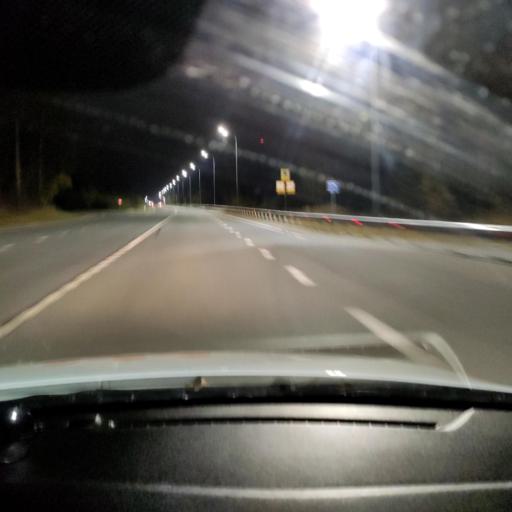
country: RU
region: Tatarstan
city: Stolbishchi
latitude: 55.6348
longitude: 49.1046
